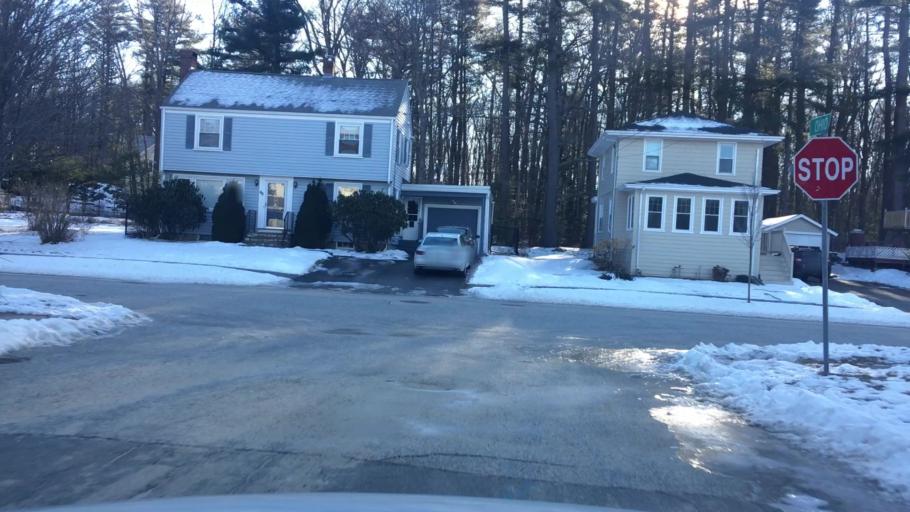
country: US
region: Maine
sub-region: Cumberland County
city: Portland
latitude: 43.6967
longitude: -70.2823
